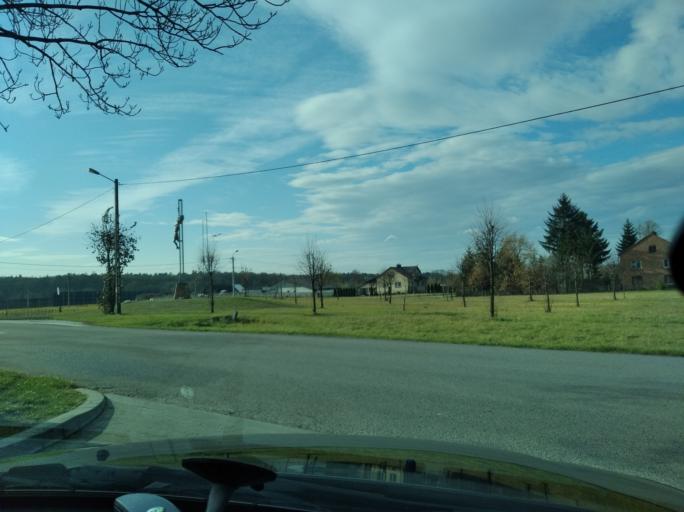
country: PL
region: Subcarpathian Voivodeship
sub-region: Powiat ropczycko-sedziszowski
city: Sedziszow Malopolski
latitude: 50.1164
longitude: 21.7344
